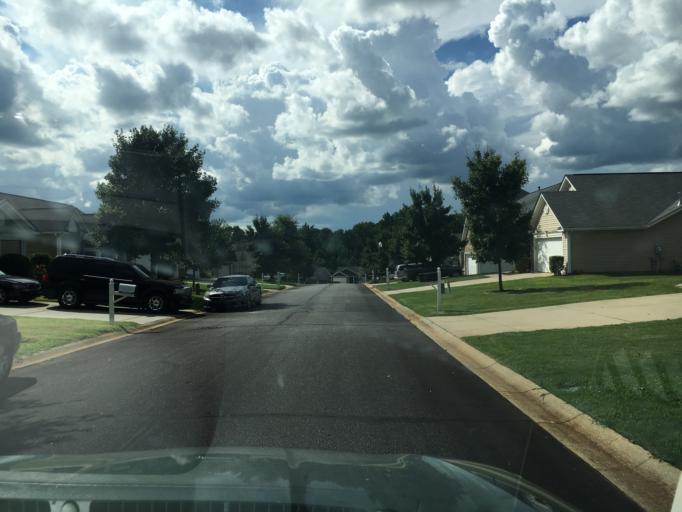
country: US
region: South Carolina
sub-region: Spartanburg County
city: Valley Falls
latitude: 35.0066
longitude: -81.9926
